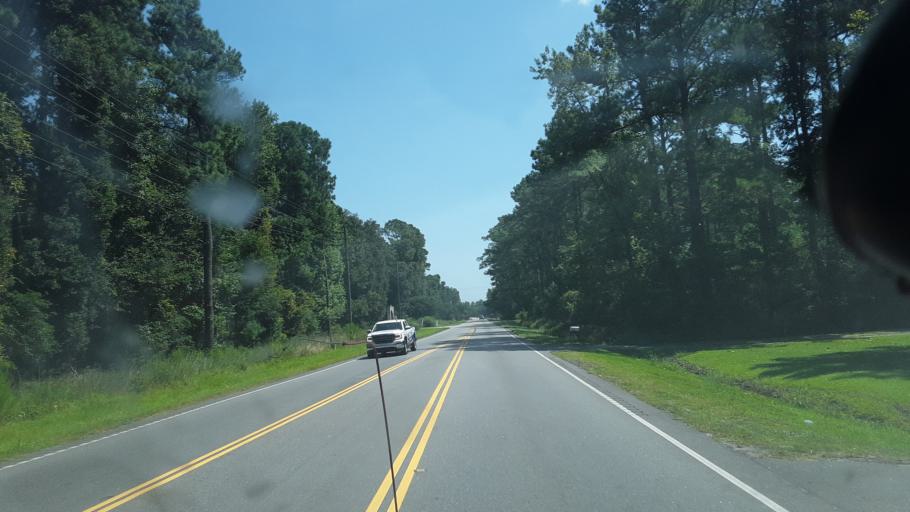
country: US
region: South Carolina
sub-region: Horry County
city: Red Hill
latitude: 33.8220
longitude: -78.9124
